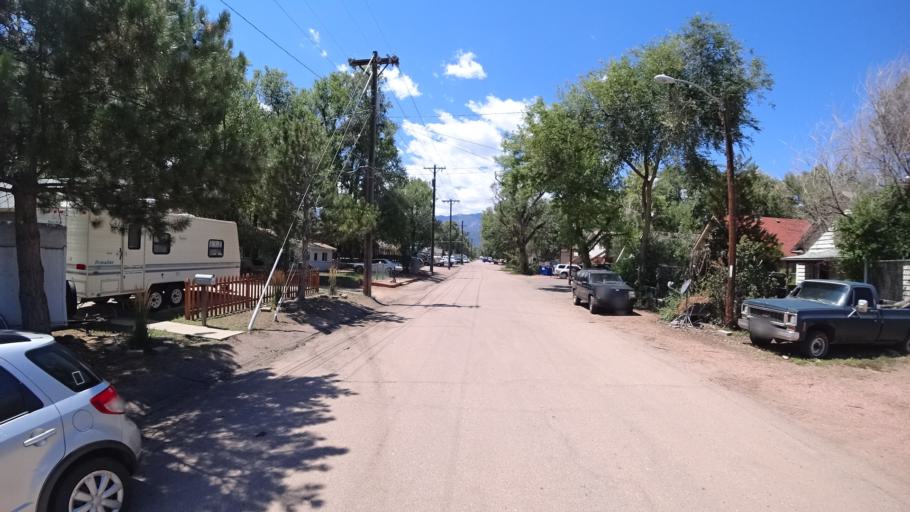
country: US
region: Colorado
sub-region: El Paso County
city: Colorado Springs
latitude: 38.8129
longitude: -104.8166
